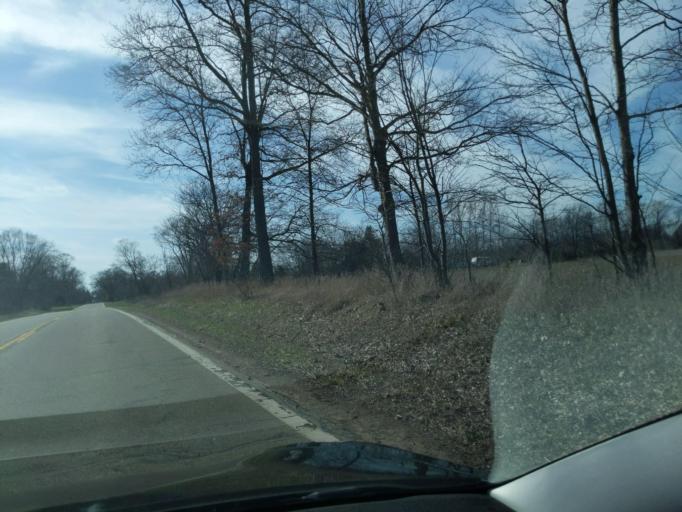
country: US
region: Michigan
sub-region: Ingham County
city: Stockbridge
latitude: 42.4538
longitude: -84.1437
